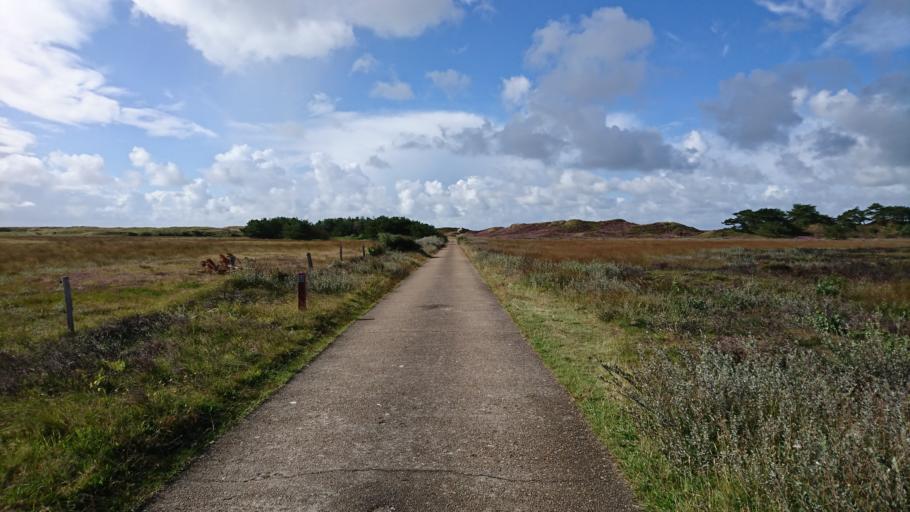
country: DK
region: South Denmark
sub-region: Fano Kommune
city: Nordby
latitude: 55.3875
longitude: 8.4179
